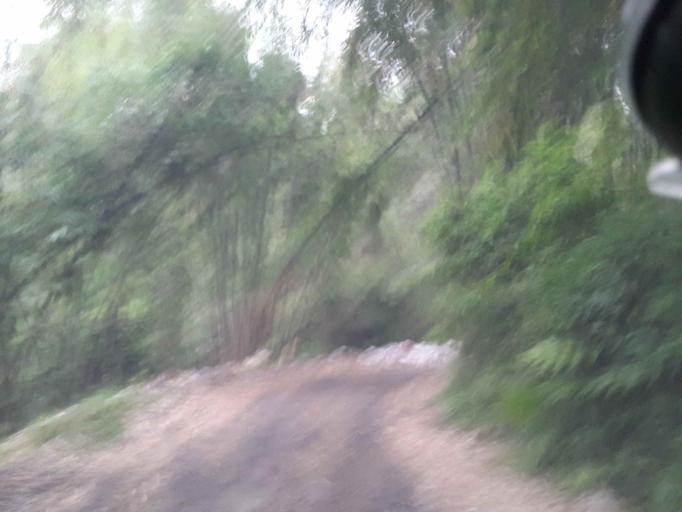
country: ID
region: East Java
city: Batu
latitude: -7.8112
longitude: 112.5327
